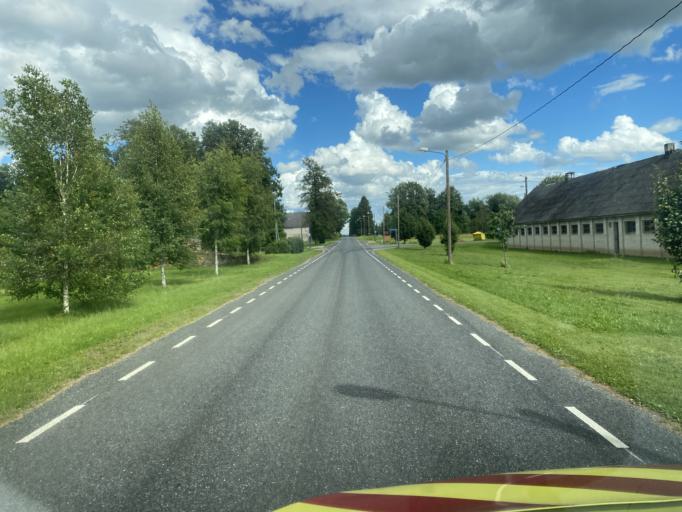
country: EE
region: Viljandimaa
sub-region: Viiratsi vald
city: Viiratsi
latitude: 58.3898
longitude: 25.7423
